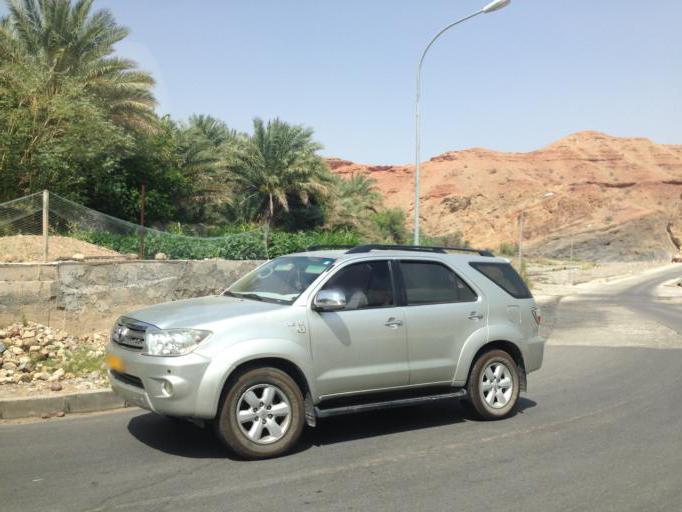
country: OM
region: Ash Sharqiyah
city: Ibra'
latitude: 23.0898
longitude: 58.8631
